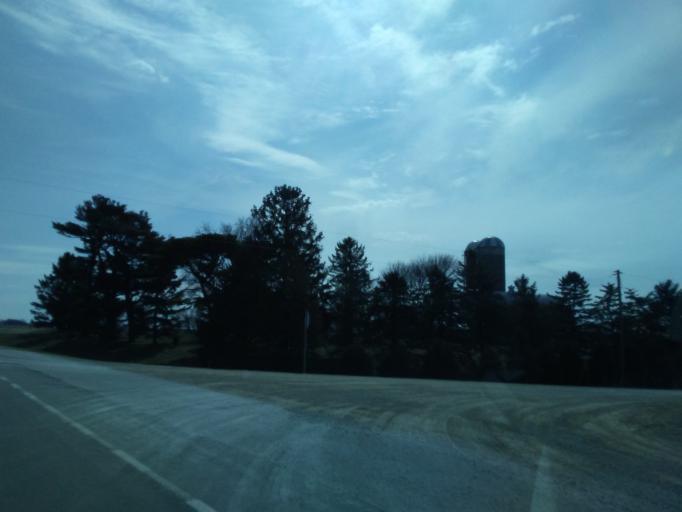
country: US
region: Iowa
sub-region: Winneshiek County
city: Decorah
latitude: 43.4144
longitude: -91.8590
